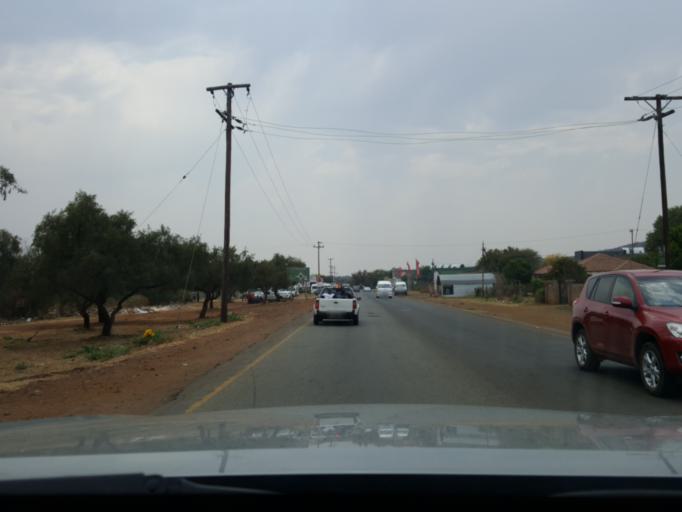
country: ZA
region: North-West
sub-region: Ngaka Modiri Molema District Municipality
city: Zeerust
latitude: -25.4957
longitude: 25.9841
